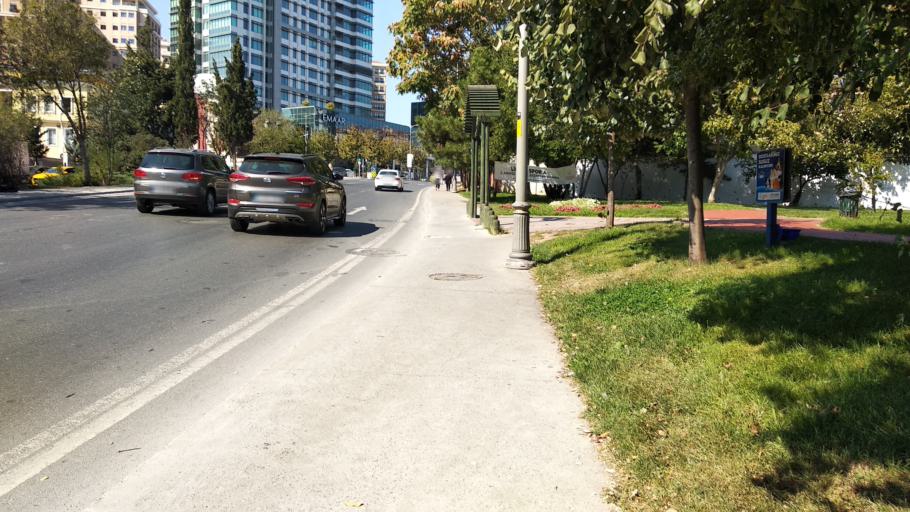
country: TR
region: Istanbul
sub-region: Atasehir
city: Atasehir
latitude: 41.0013
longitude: 29.0733
